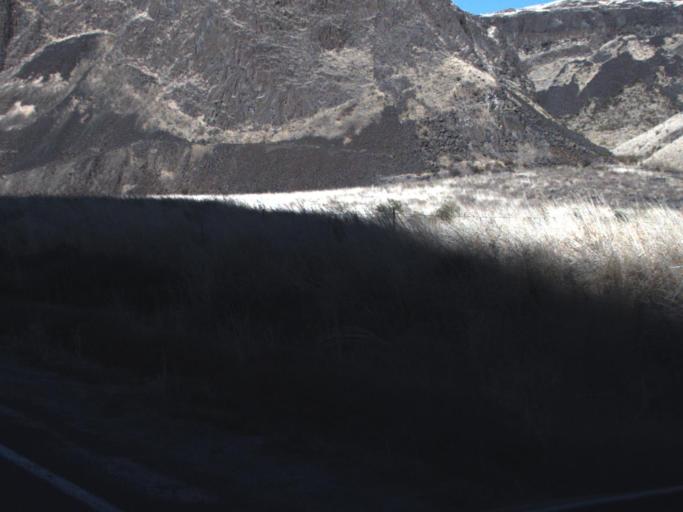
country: US
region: Washington
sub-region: Franklin County
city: Connell
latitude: 46.5924
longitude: -118.5459
